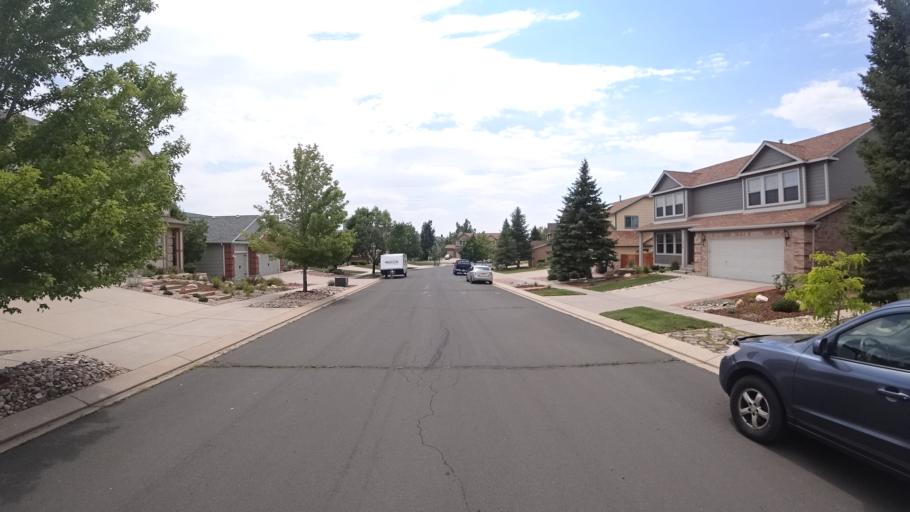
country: US
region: Colorado
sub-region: El Paso County
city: Black Forest
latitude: 38.9628
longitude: -104.7751
